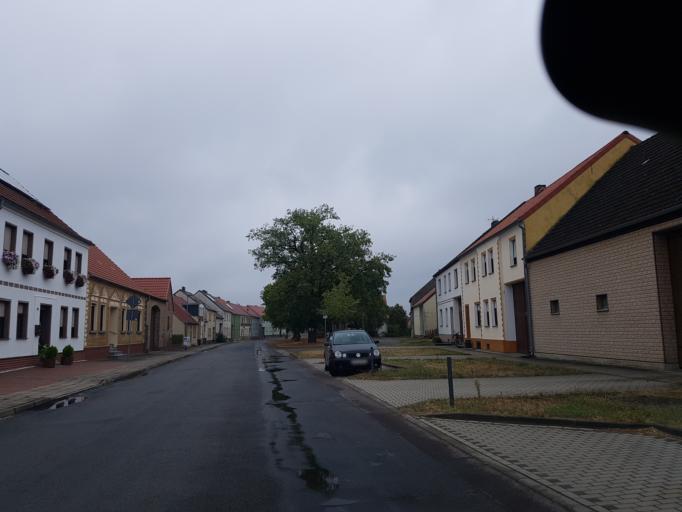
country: DE
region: Brandenburg
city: Gorzke
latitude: 52.1387
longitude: 12.3111
